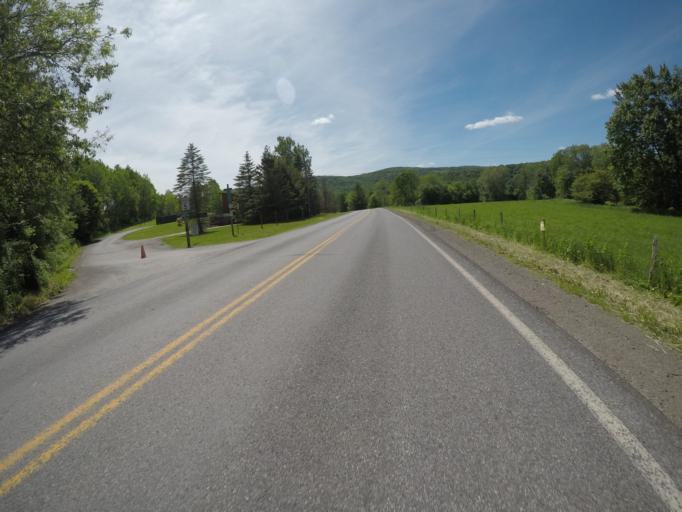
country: US
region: New York
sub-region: Delaware County
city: Delhi
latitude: 42.1641
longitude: -74.7941
